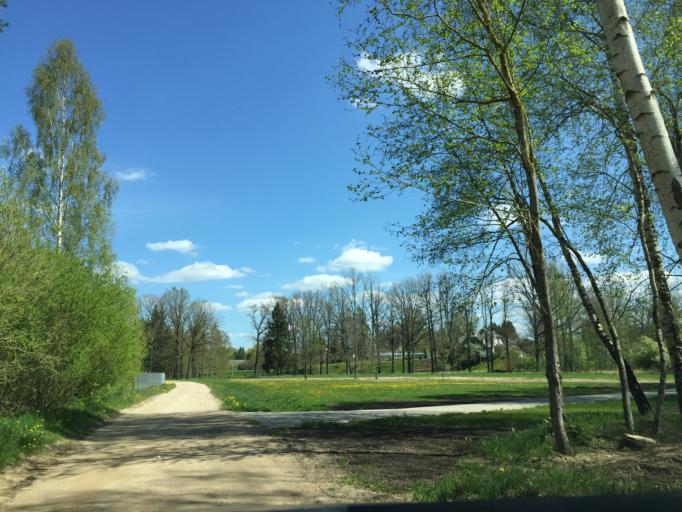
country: LV
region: Vecumnieki
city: Vecumnieki
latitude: 56.5999
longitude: 24.5251
